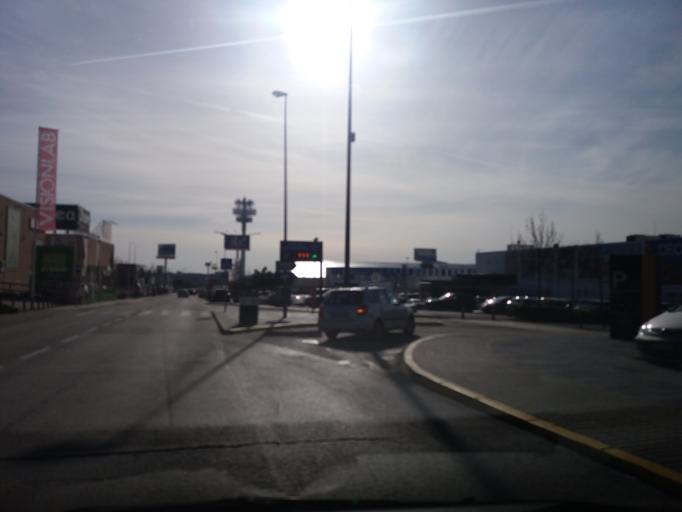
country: ES
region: Madrid
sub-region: Provincia de Madrid
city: Majadahonda
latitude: 40.4551
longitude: -3.8731
